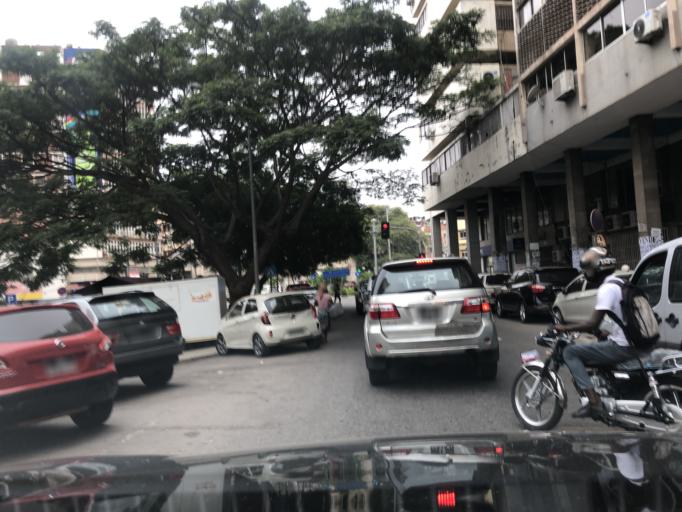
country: AO
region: Luanda
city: Luanda
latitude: -8.8181
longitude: 13.2308
